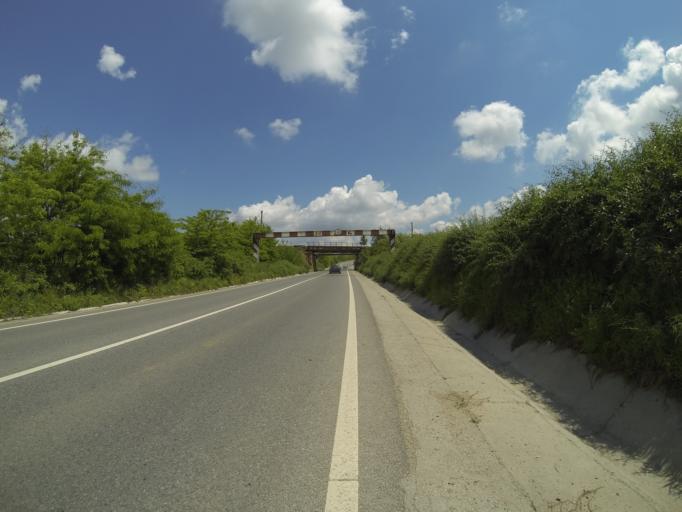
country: RO
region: Dolj
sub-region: Comuna Carcea
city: Carcea
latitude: 44.2662
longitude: 23.8878
